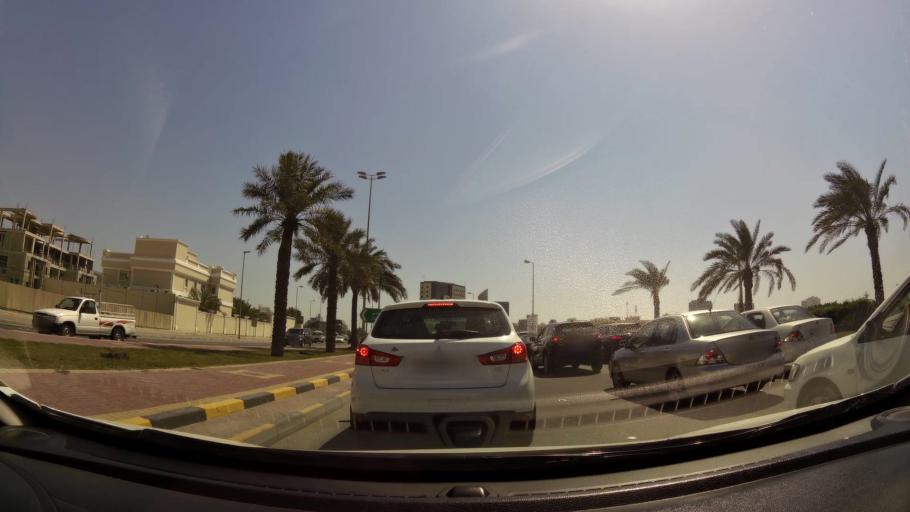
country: BH
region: Manama
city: Manama
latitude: 26.2104
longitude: 50.5970
